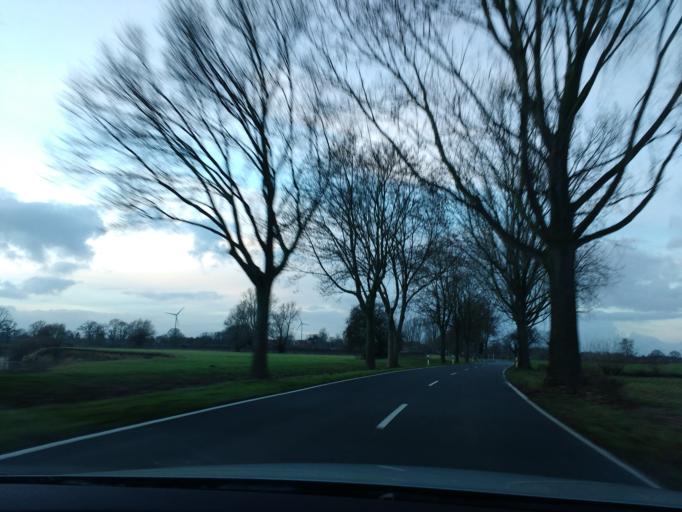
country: DE
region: Lower Saxony
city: Schwarmstedt
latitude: 52.6382
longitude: 9.5861
